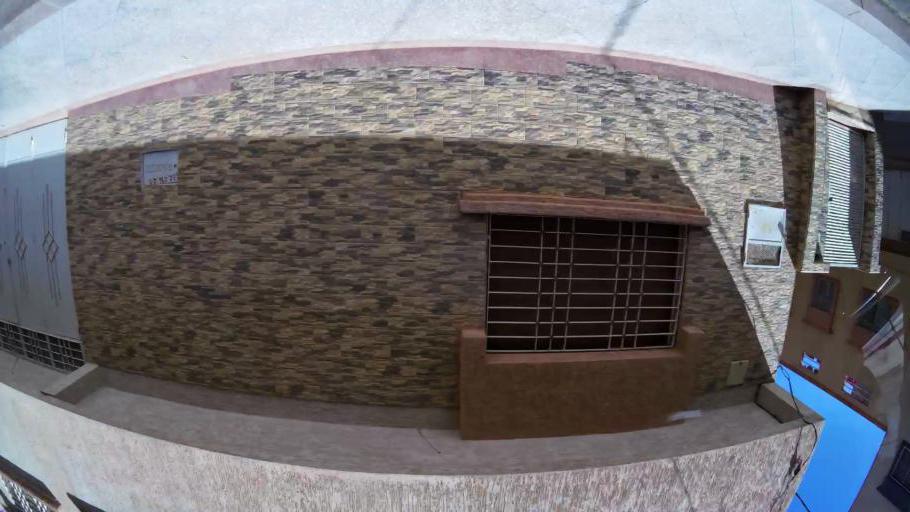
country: MA
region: Oriental
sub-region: Oujda-Angad
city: Oujda
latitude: 34.6558
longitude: -1.9182
